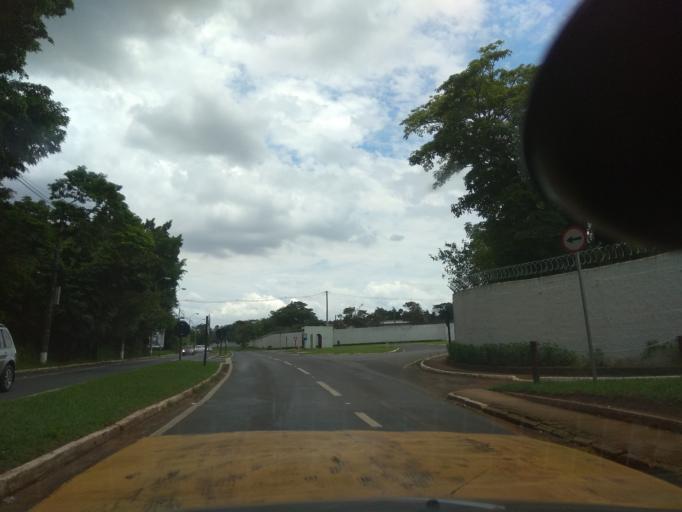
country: BR
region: Sao Paulo
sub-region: Paulinia
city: Paulinia
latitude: -22.7947
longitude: -47.0796
